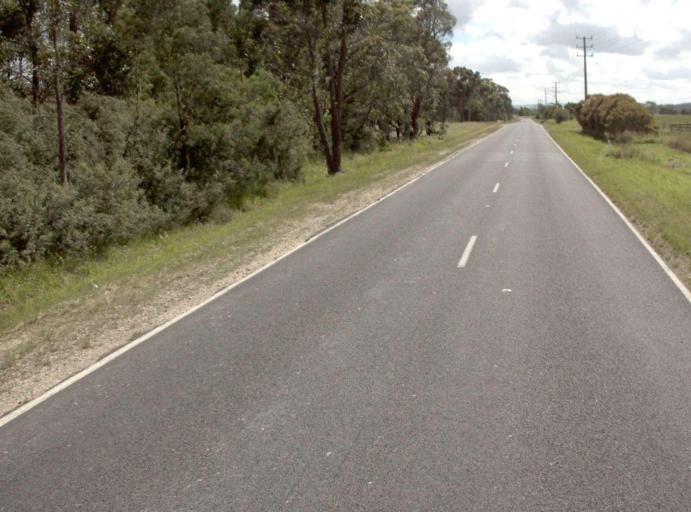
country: AU
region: Victoria
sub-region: Latrobe
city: Traralgon
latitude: -38.1352
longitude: 146.5454
